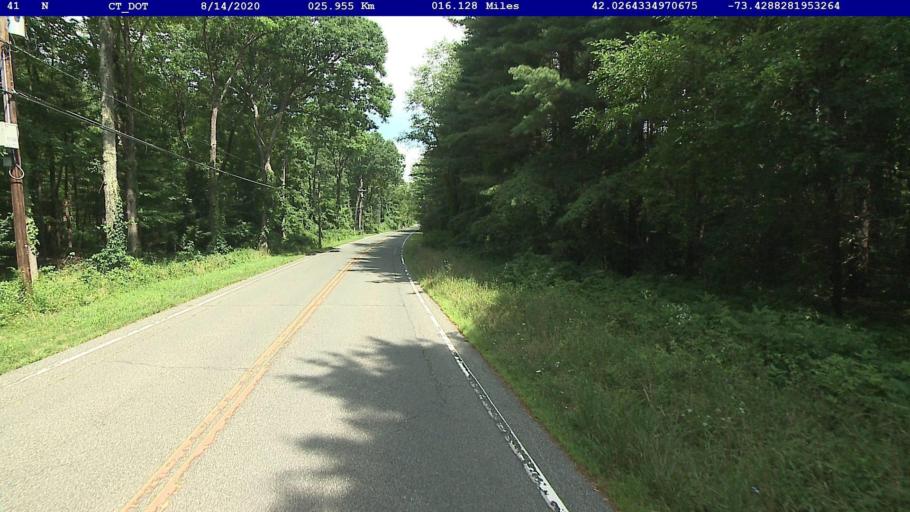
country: US
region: Connecticut
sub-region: Litchfield County
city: Canaan
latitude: 42.0264
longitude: -73.4288
